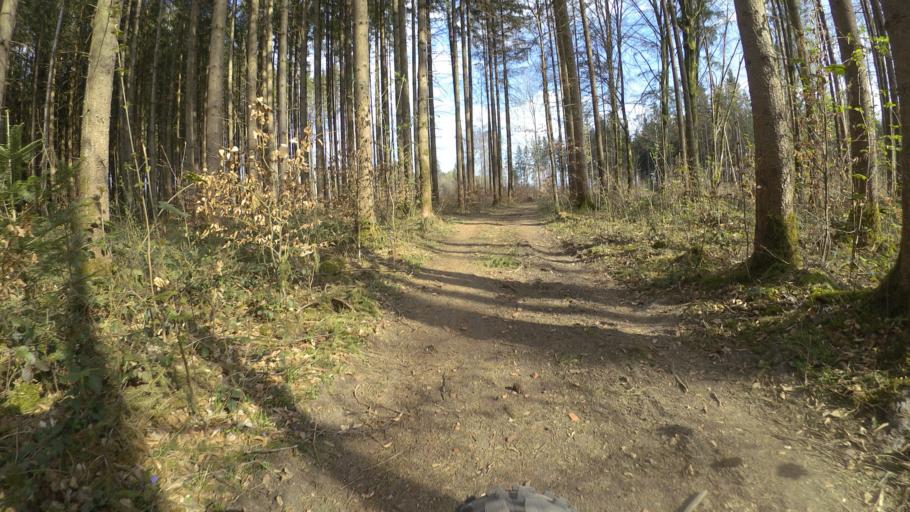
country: DE
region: Bavaria
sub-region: Upper Bavaria
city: Chieming
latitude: 47.9179
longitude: 12.5394
